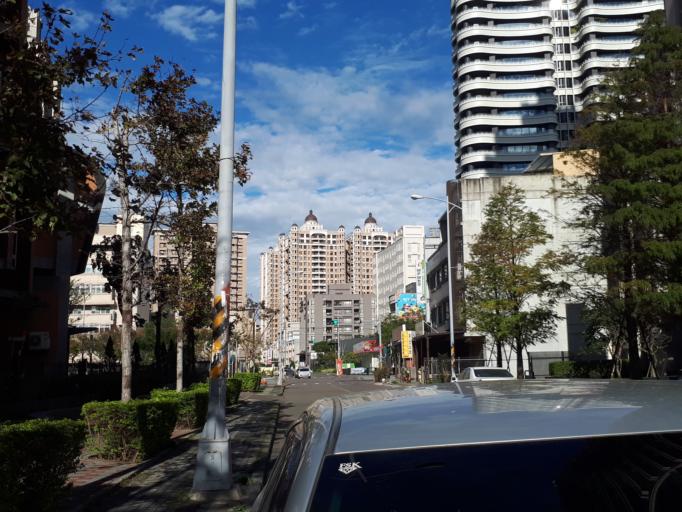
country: TW
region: Taiwan
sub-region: Hsinchu
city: Zhubei
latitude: 24.8045
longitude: 121.0331
